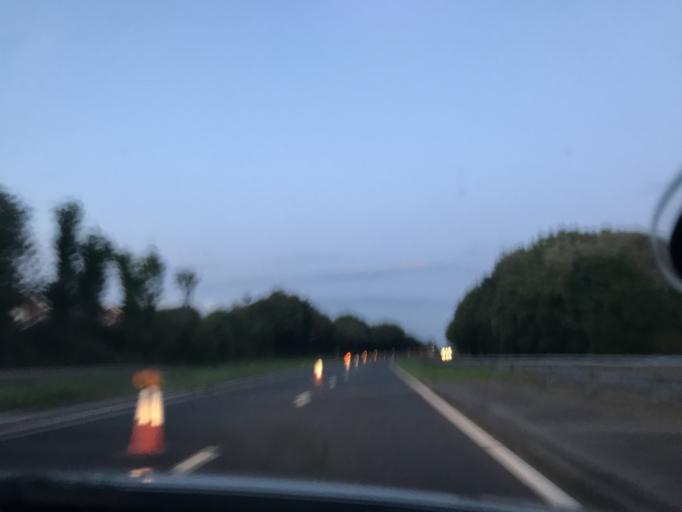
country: GB
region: England
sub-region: Cheshire West and Chester
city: Hartford
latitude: 53.2388
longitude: -2.5488
